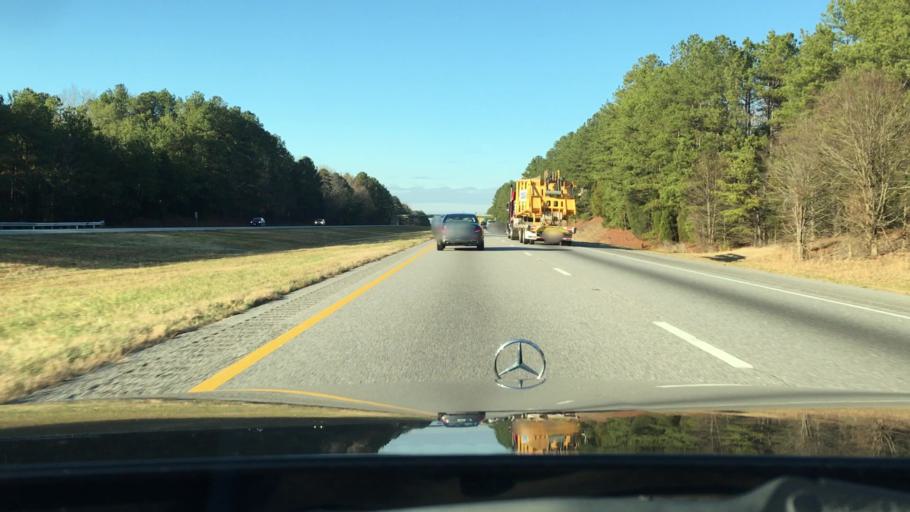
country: US
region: South Carolina
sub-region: Chester County
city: Eureka Mill
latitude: 34.6916
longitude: -81.0295
